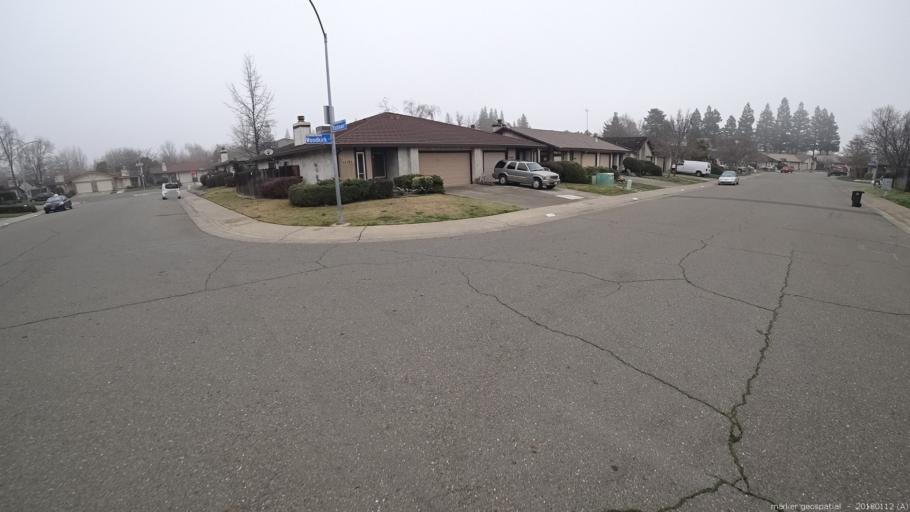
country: US
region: California
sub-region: Sacramento County
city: Gold River
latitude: 38.6109
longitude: -121.2733
